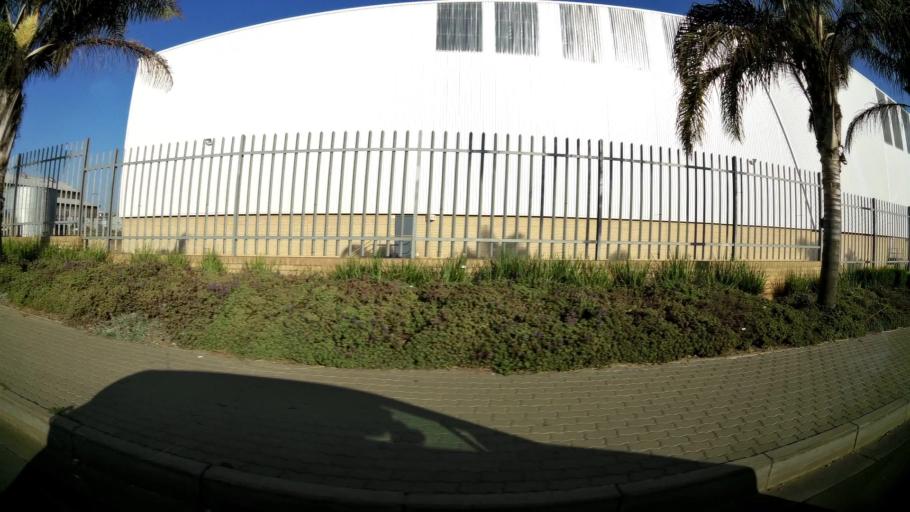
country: ZA
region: Gauteng
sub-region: City of Johannesburg Metropolitan Municipality
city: Modderfontein
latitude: -26.1577
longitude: 28.1891
